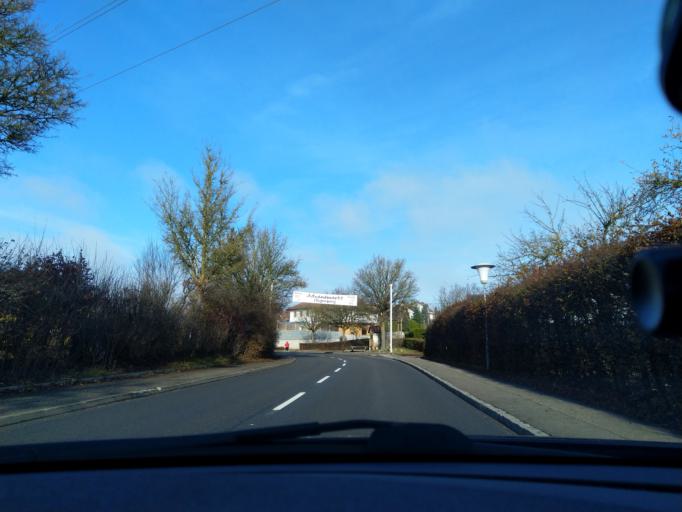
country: AT
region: Upper Austria
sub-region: Politischer Bezirk Urfahr-Umgebung
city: Engerwitzdorf
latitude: 48.3642
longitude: 14.5239
